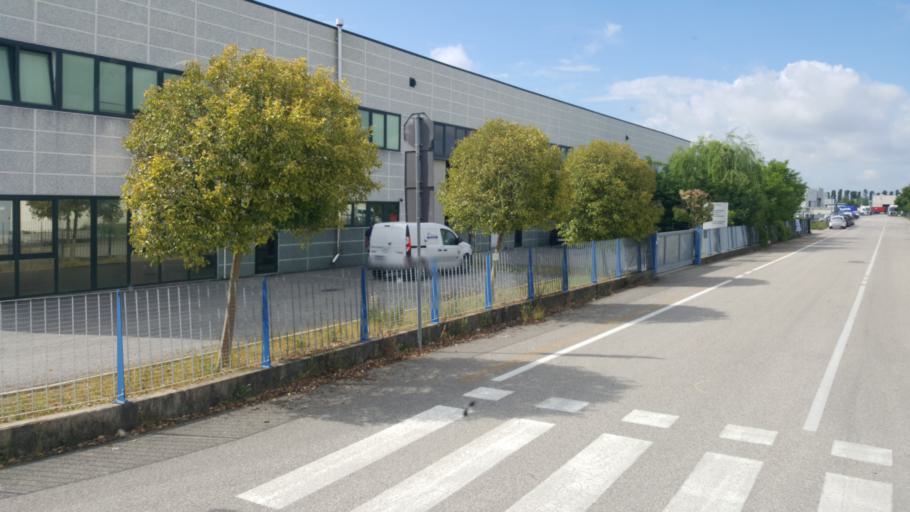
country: IT
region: Veneto
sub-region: Provincia di Venezia
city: Noventa di Piave
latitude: 45.6754
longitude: 12.5615
